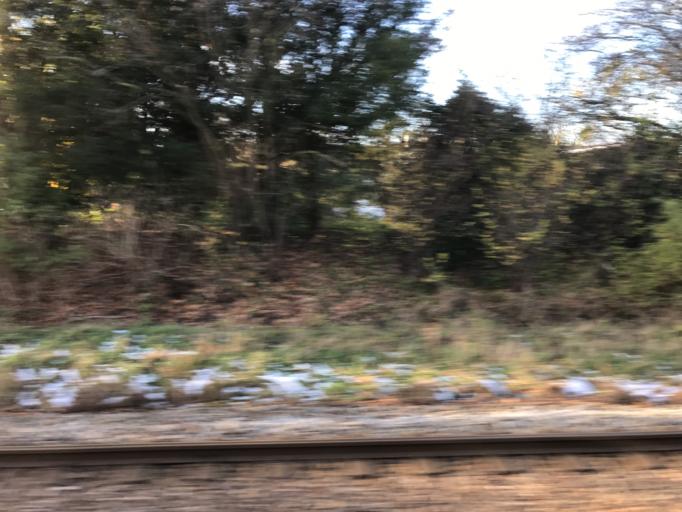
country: DK
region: Zealand
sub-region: Stevns Kommune
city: Harlev
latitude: 55.3532
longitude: 12.2281
